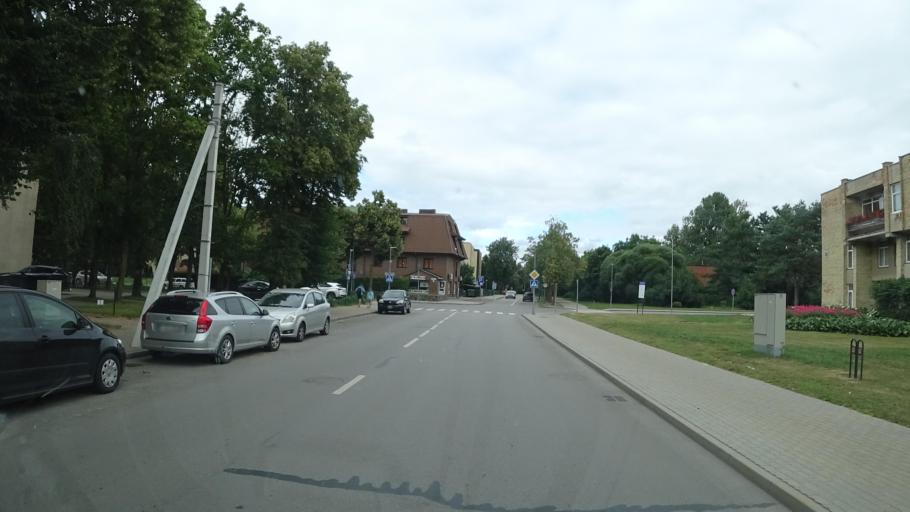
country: LT
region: Klaipedos apskritis
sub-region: Klaipeda
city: Palanga
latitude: 55.9248
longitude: 21.0753
